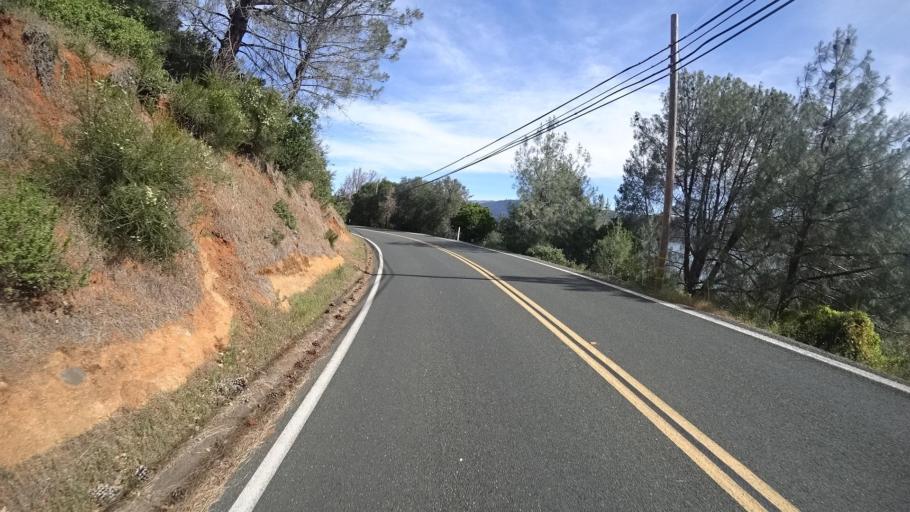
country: US
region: California
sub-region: Lake County
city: Soda Bay
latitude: 38.9949
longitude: -122.7503
